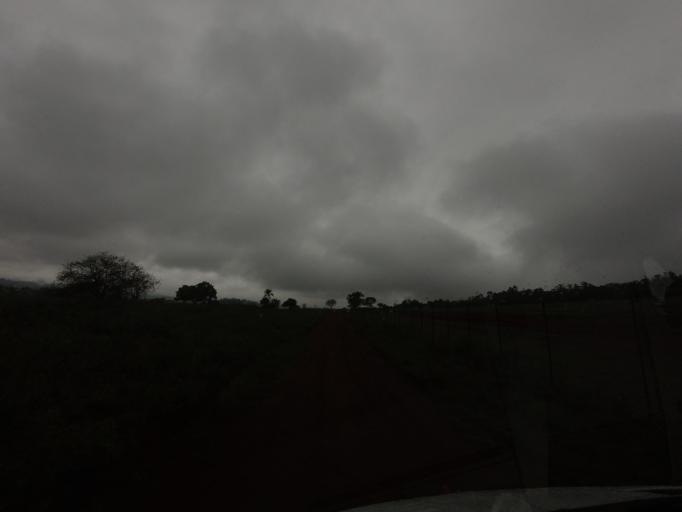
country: SZ
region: Hhohho
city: Lobamba
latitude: -26.4697
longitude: 31.1856
